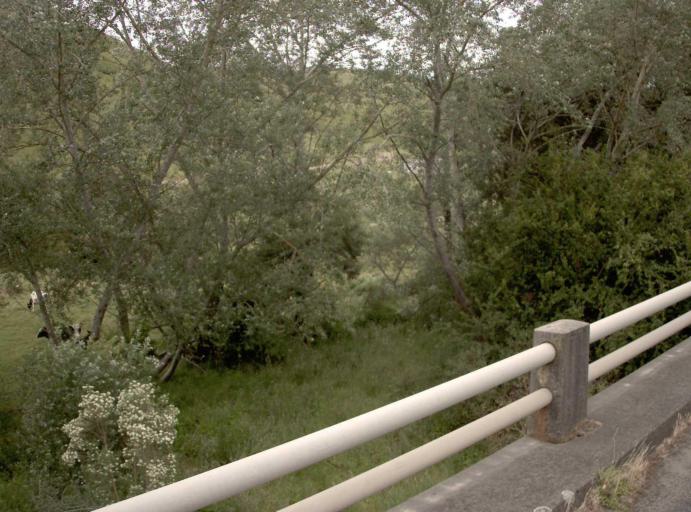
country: AU
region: Victoria
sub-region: Bass Coast
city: North Wonthaggi
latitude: -38.3742
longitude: 145.7192
